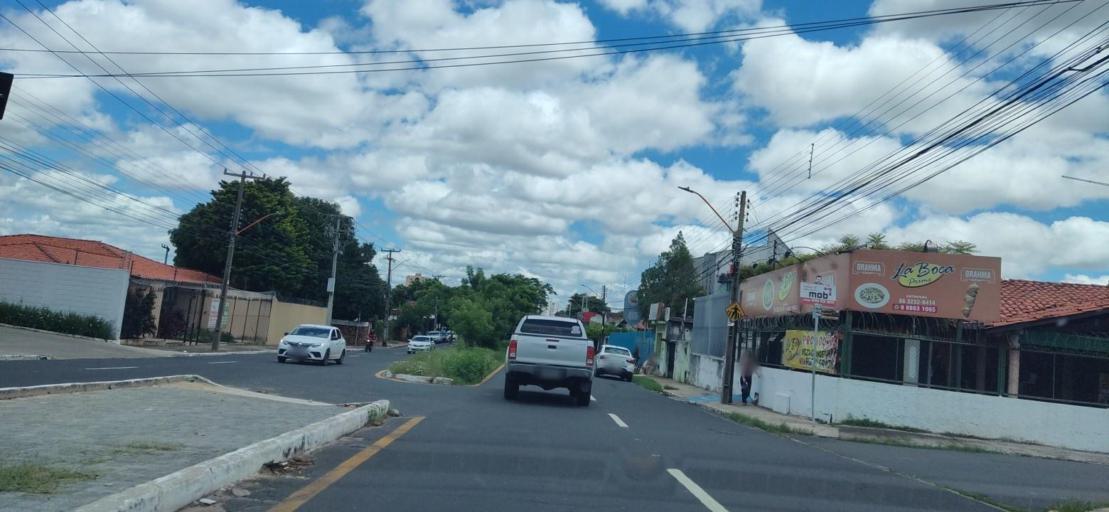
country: BR
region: Piaui
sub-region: Teresina
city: Teresina
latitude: -5.0648
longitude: -42.7628
